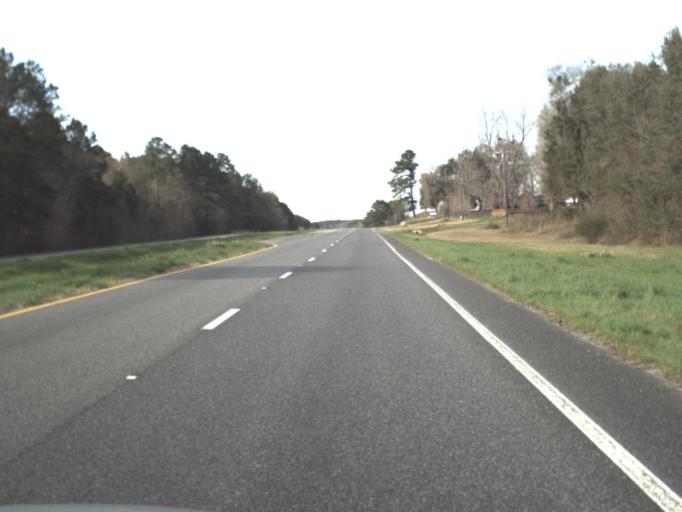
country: US
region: Florida
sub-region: Jefferson County
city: Monticello
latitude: 30.6165
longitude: -83.8722
